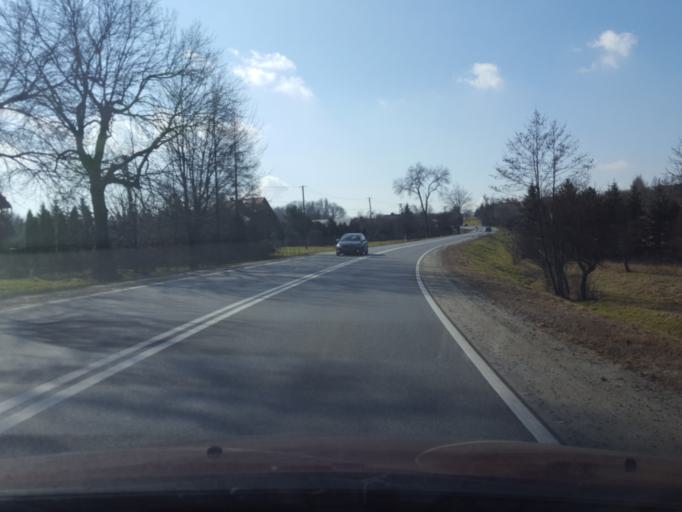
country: PL
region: Lesser Poland Voivodeship
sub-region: Powiat brzeski
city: Gnojnik
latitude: 49.8784
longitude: 20.6177
